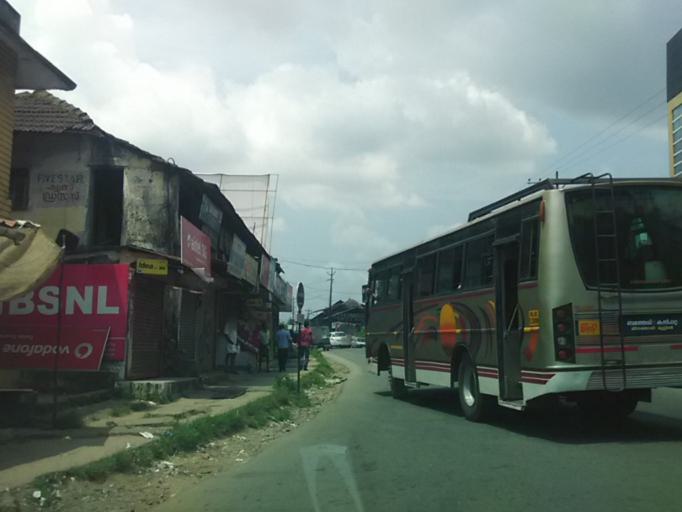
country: IN
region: Kerala
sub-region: Wayanad
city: Kalpetta
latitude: 11.6058
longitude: 76.0838
